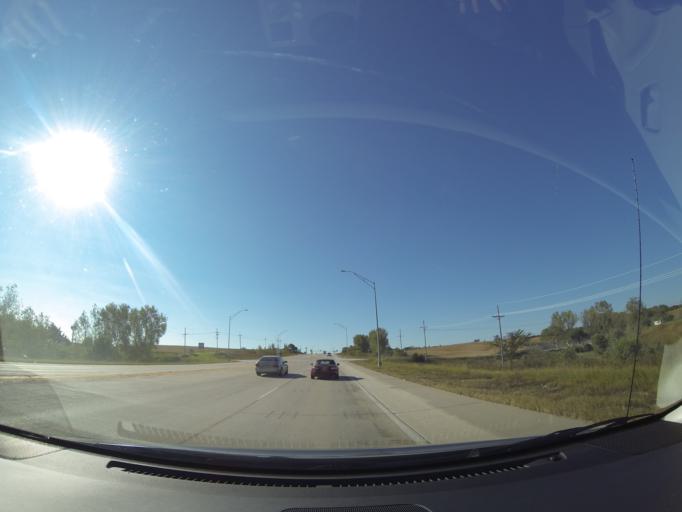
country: US
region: Nebraska
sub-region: Sarpy County
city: Gretna
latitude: 41.1041
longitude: -96.2534
